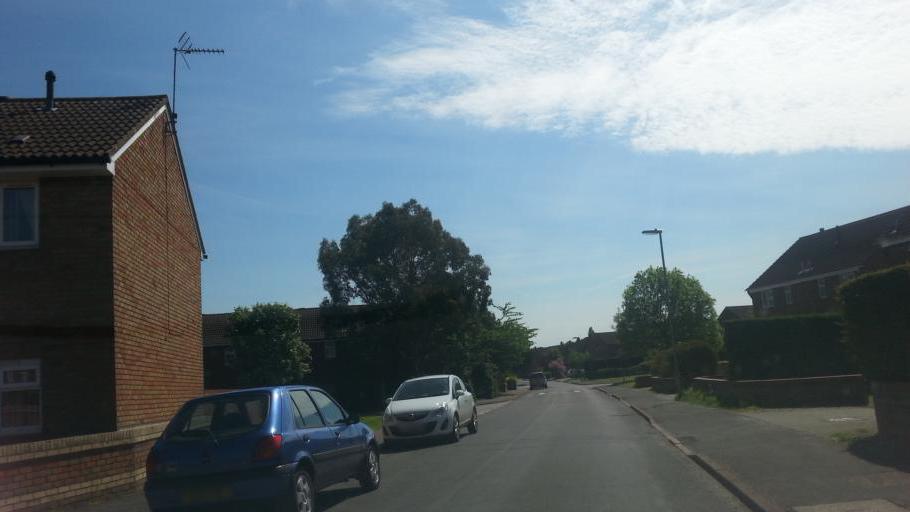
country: GB
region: England
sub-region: Cambridgeshire
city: Warboys
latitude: 52.4064
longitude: -0.0819
